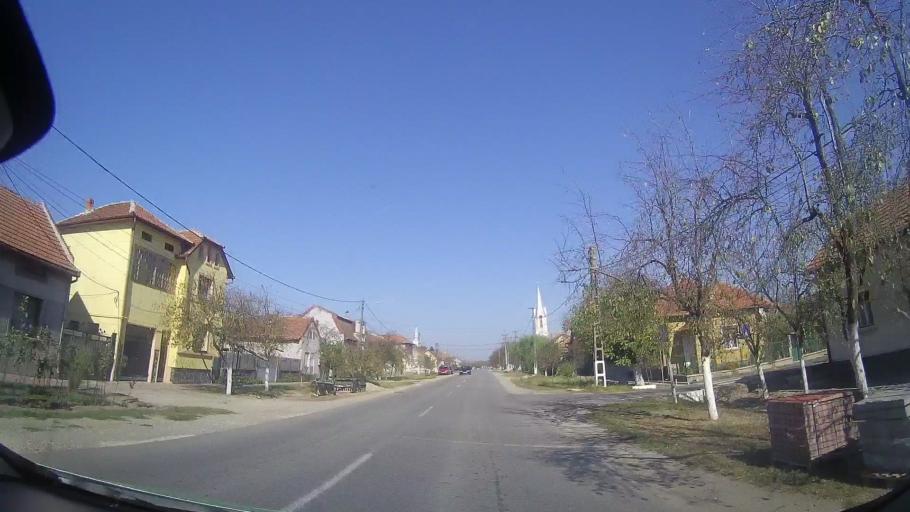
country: RO
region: Timis
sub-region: Comuna Costeiu
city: Costeiu
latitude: 45.7402
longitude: 21.8488
